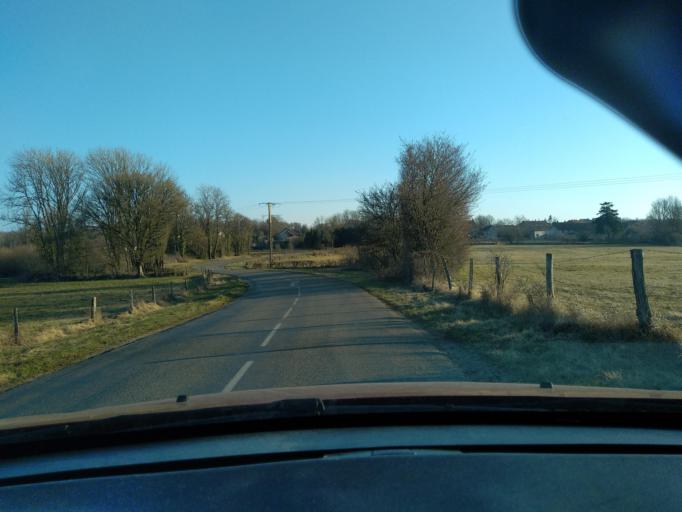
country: FR
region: Franche-Comte
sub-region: Departement du Jura
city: Perrigny
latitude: 46.6689
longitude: 5.6522
